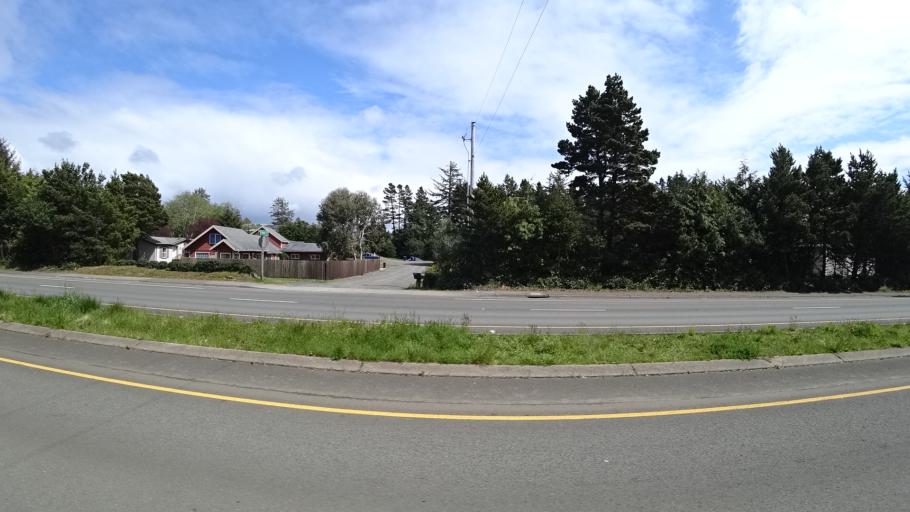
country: US
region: Oregon
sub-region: Lincoln County
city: Lincoln Beach
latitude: 44.8531
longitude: -124.0426
